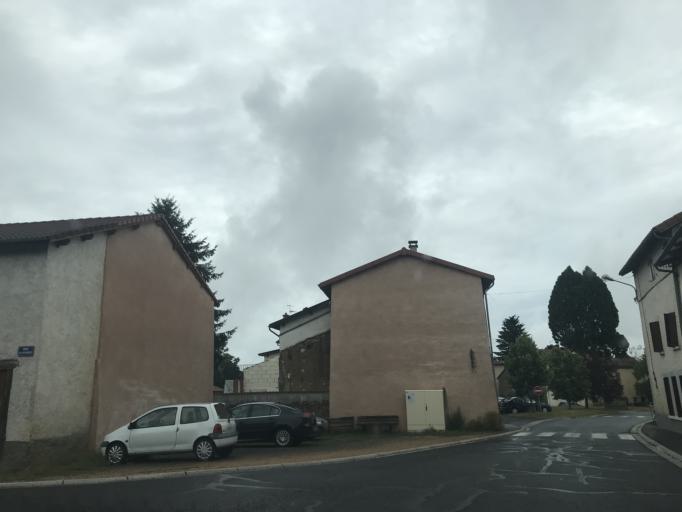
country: FR
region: Auvergne
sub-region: Departement du Puy-de-Dome
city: Arlanc
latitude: 45.4197
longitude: 3.7282
